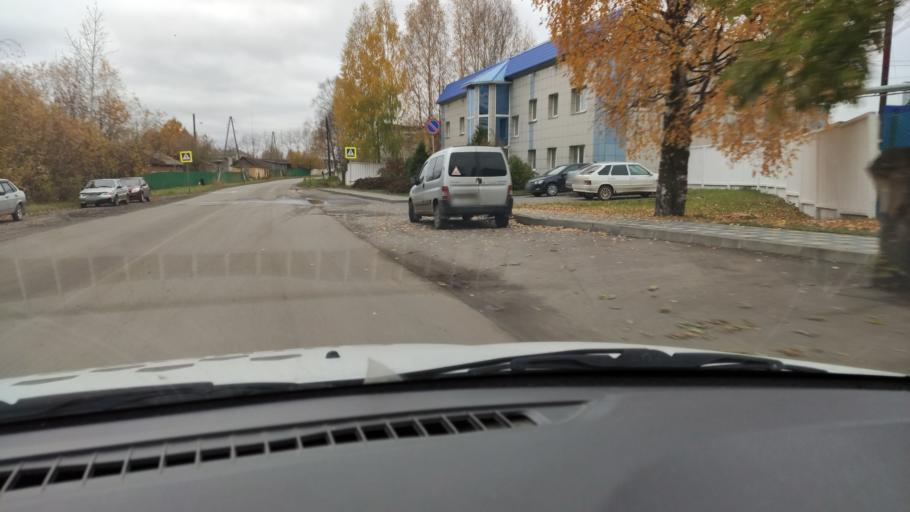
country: RU
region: Kirov
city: Slobodskoy
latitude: 58.7207
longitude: 50.1748
